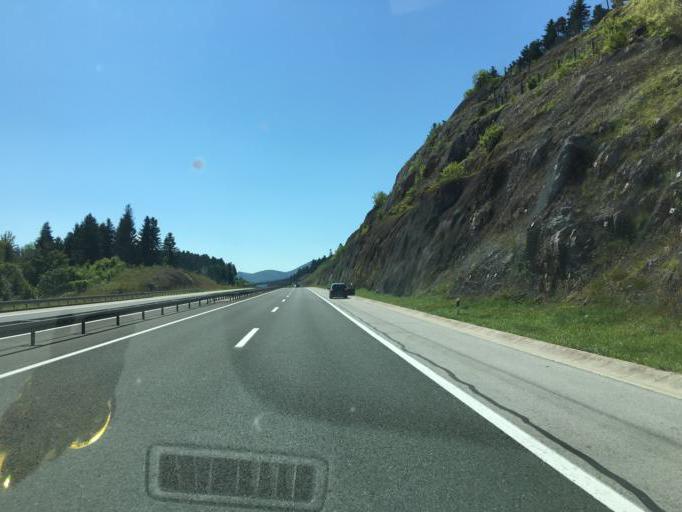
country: HR
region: Licko-Senjska
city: Otocac
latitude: 44.8533
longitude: 15.2262
